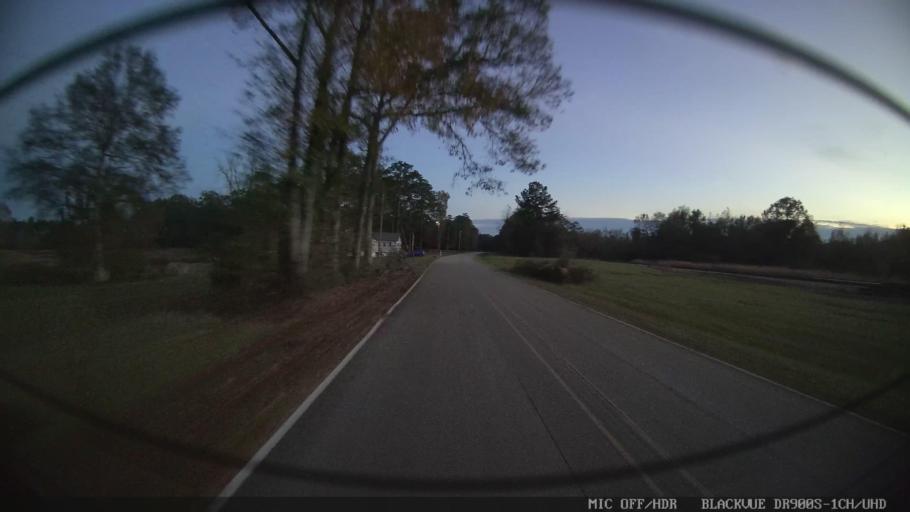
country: US
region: Mississippi
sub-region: Perry County
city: New Augusta
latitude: 31.1609
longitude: -89.2124
